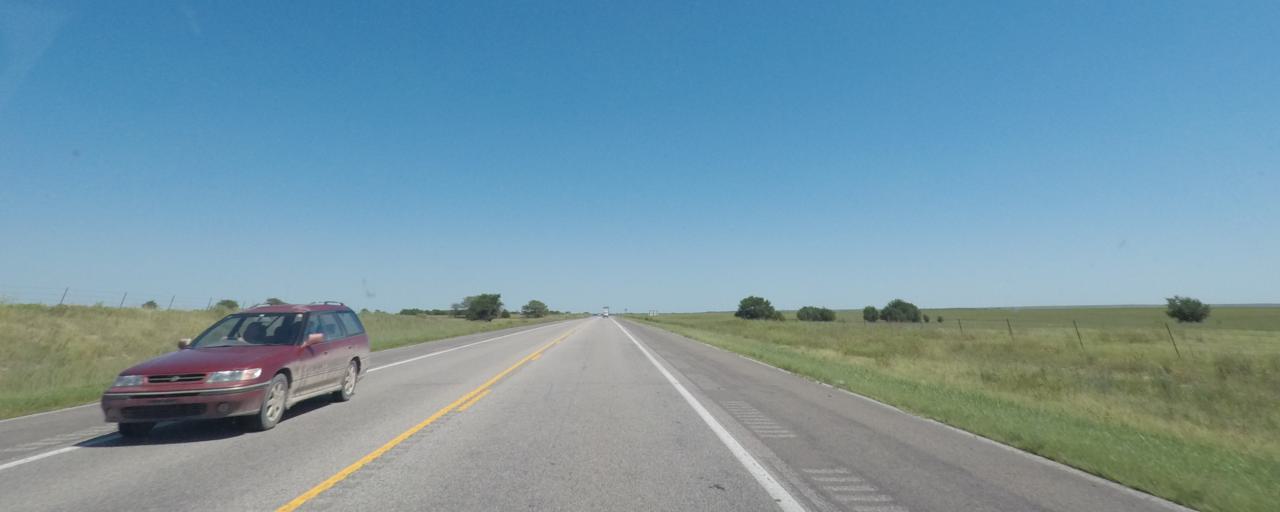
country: US
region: Kansas
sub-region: Chase County
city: Cottonwood Falls
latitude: 38.4057
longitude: -96.4783
